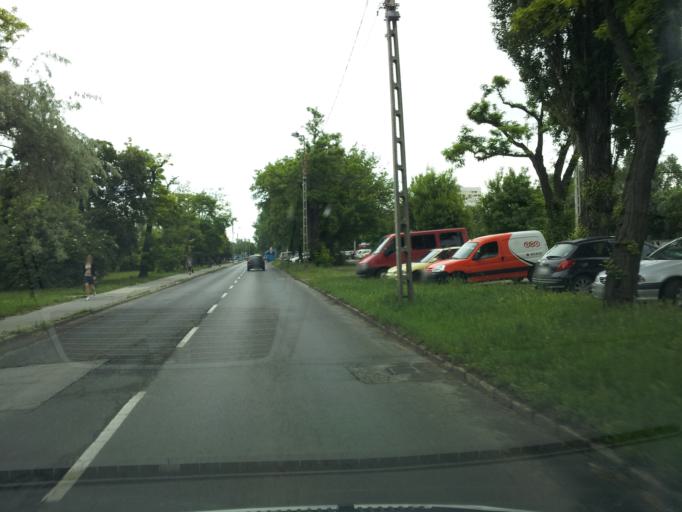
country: HU
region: Pest
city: Budakalasz
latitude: 47.5962
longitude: 19.0526
